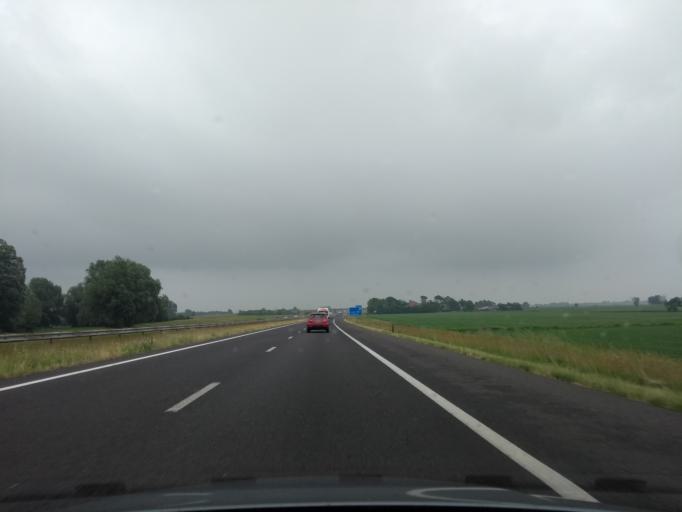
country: NL
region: Friesland
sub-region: Gemeente Skarsterlan
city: Joure
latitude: 52.9690
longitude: 5.7626
